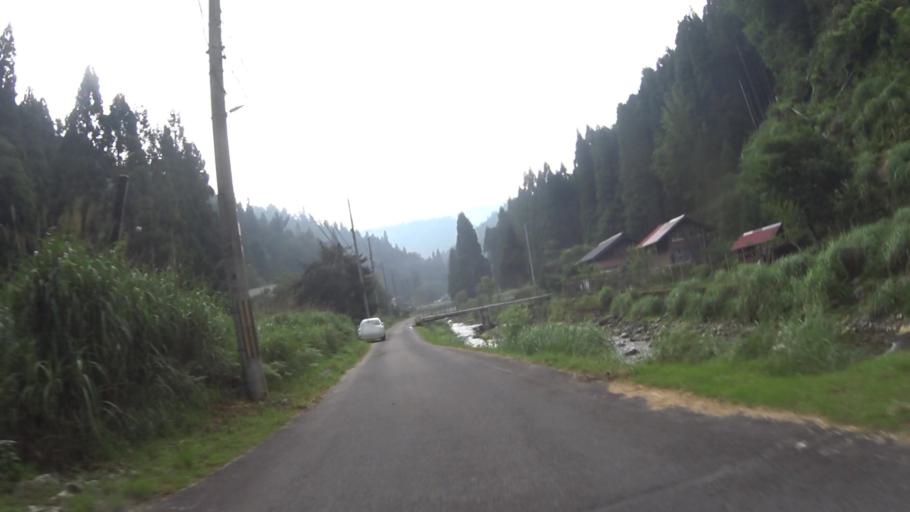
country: JP
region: Shiga Prefecture
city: Kitahama
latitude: 35.2564
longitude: 135.7663
